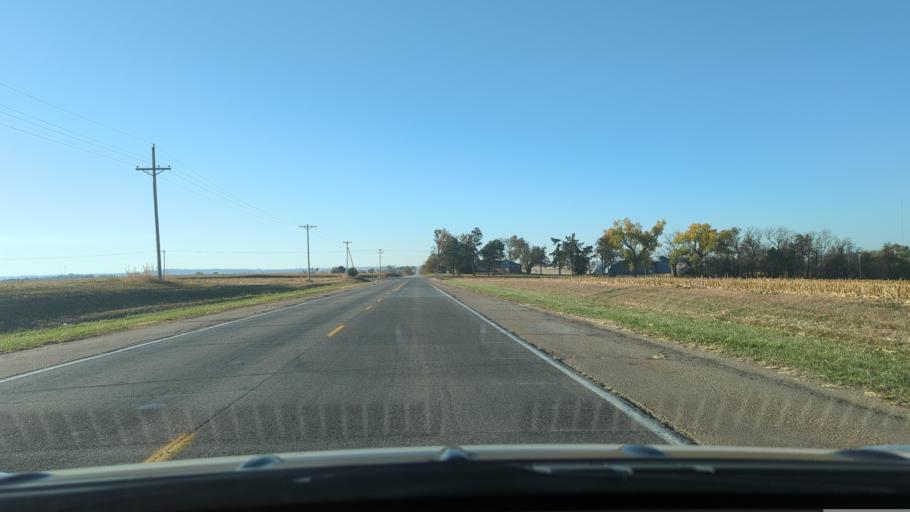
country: US
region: Nebraska
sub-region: Sarpy County
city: Springfield
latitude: 41.0912
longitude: -96.1577
